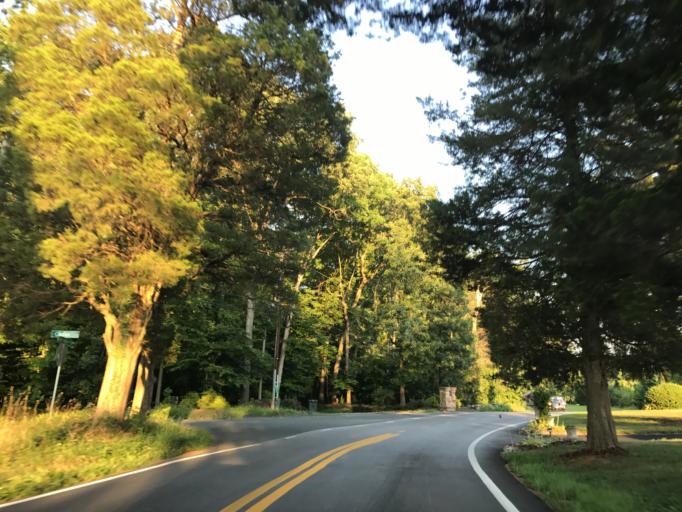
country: US
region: Maryland
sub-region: Baltimore County
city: Kingsville
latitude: 39.4311
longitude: -76.4203
